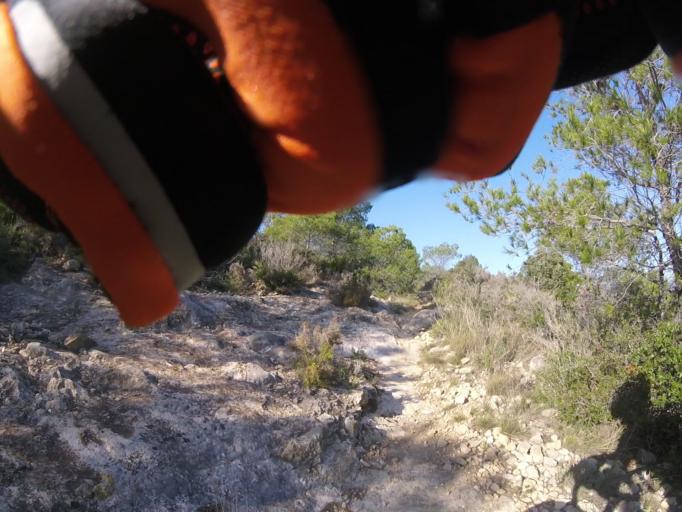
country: ES
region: Valencia
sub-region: Provincia de Castello
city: Santa Magdalena de Pulpis
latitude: 40.2982
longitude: 0.3312
